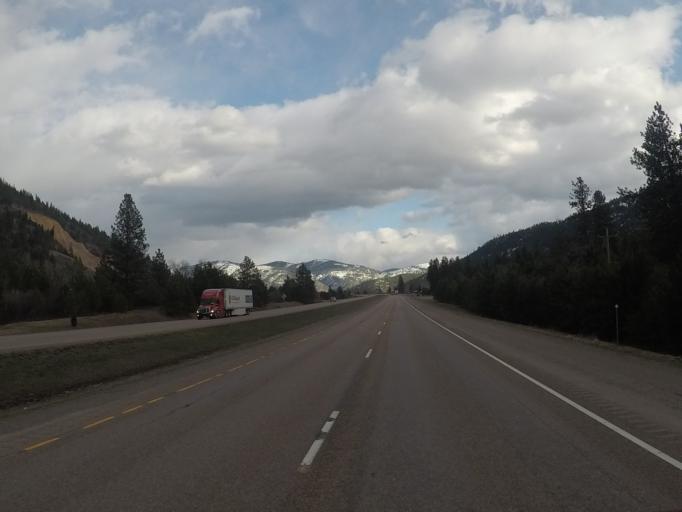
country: US
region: Montana
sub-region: Missoula County
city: Clinton
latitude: 46.8045
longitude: -113.7767
